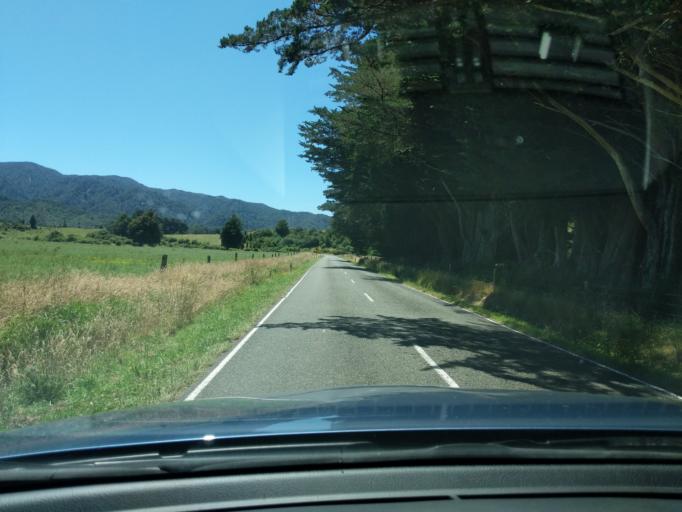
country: NZ
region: Tasman
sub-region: Tasman District
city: Takaka
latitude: -40.7597
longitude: 172.5633
